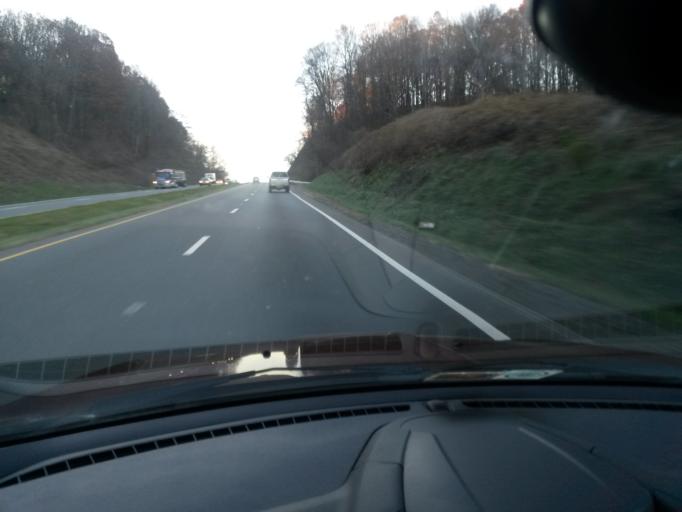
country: US
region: Virginia
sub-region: Roanoke County
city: Narrows
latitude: 37.0998
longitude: -79.9410
